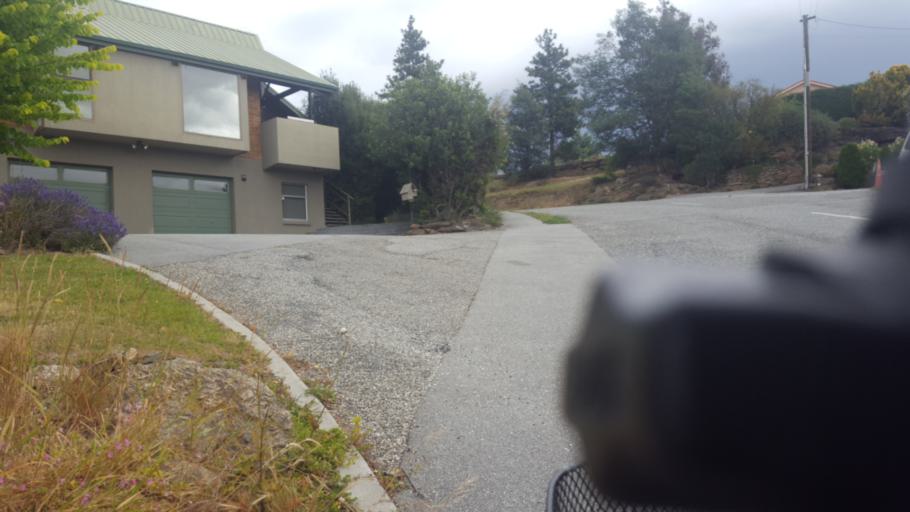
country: NZ
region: Otago
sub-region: Queenstown-Lakes District
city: Wanaka
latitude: -45.2632
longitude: 169.3775
